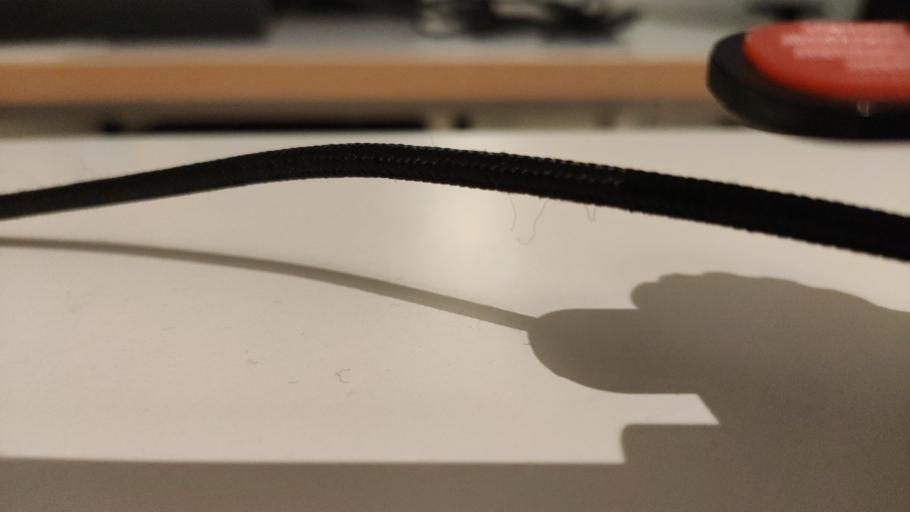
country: RU
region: Moskovskaya
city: Rogachevo
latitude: 56.4333
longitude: 37.1807
